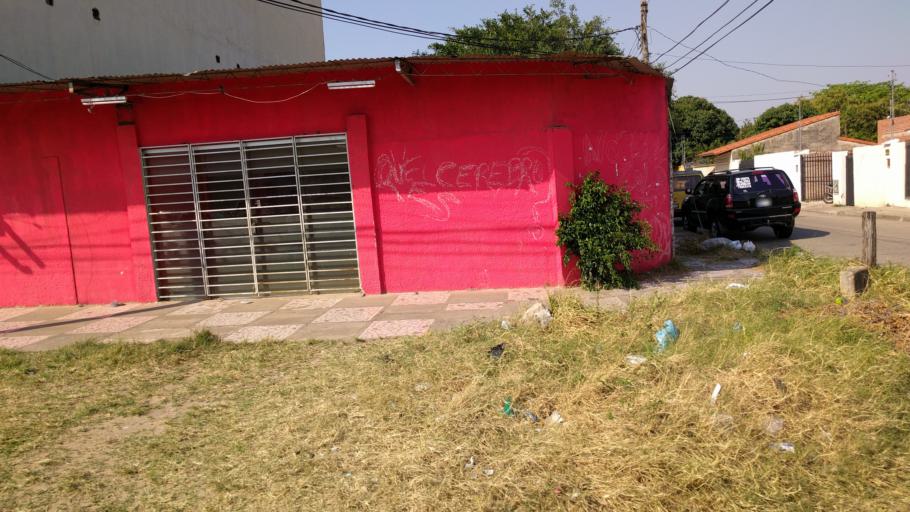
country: BO
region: Santa Cruz
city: Santa Cruz de la Sierra
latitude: -17.7740
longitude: -63.1540
